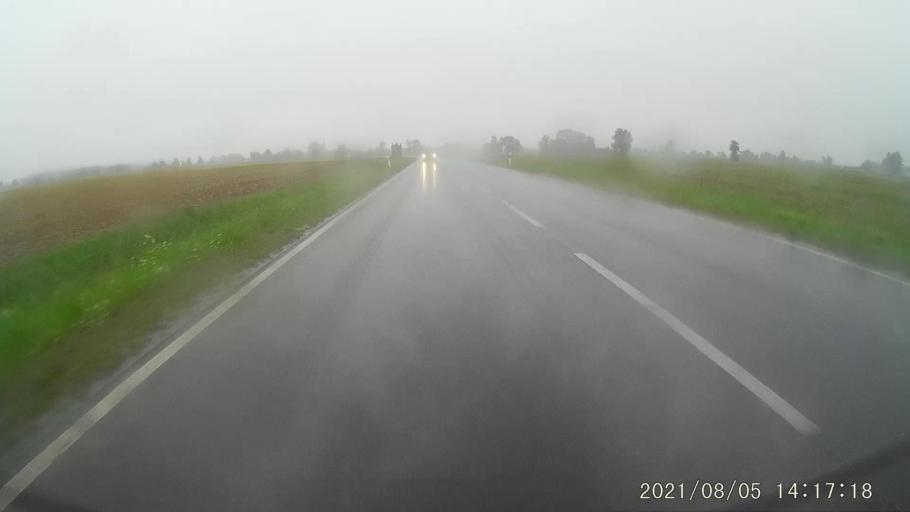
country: PL
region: Opole Voivodeship
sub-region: Powiat prudnicki
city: Biala
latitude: 50.4602
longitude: 17.7077
